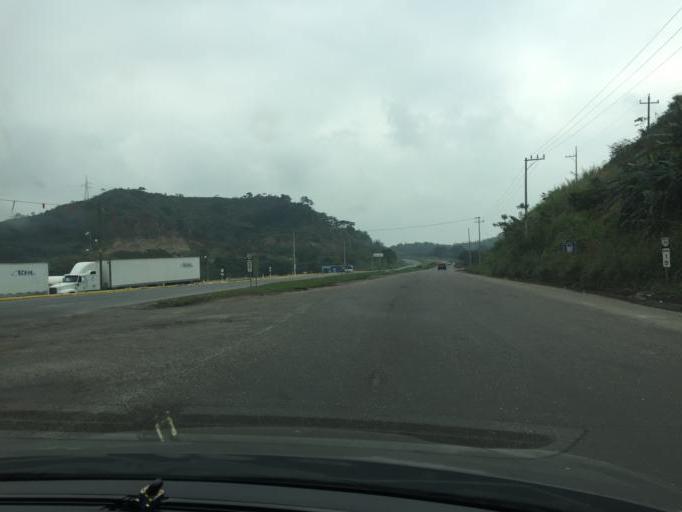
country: MX
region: Veracruz
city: Villa Nanchital
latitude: 18.0722
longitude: -94.3145
